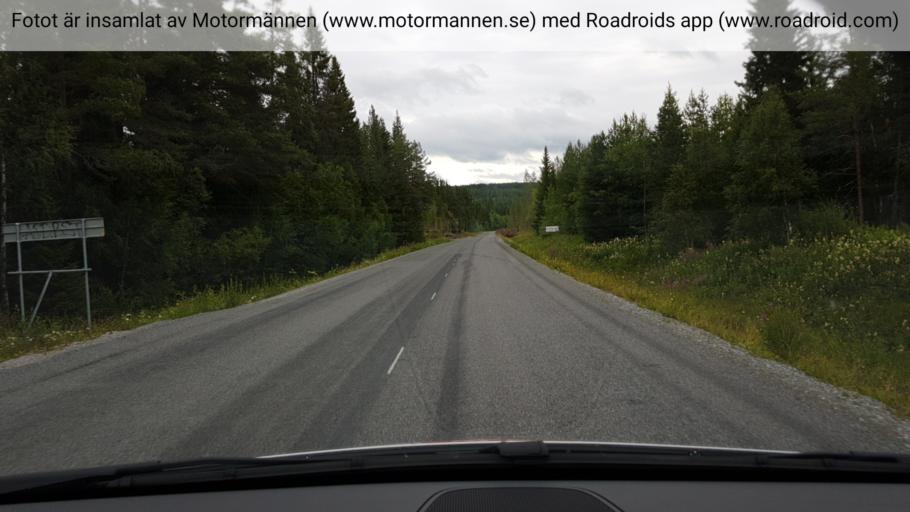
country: SE
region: Jaemtland
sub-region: Krokoms Kommun
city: Krokom
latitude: 63.6736
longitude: 14.5630
